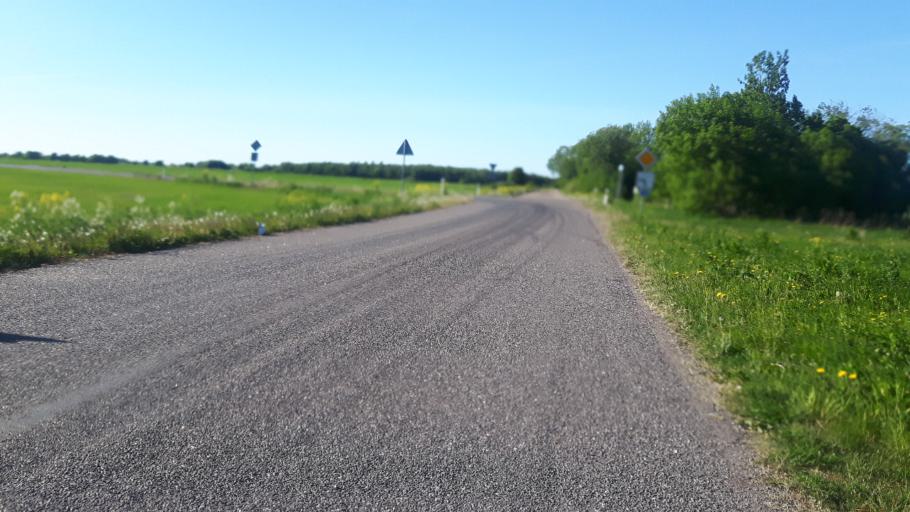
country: EE
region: Ida-Virumaa
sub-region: Kohtla-Jaerve linn
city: Kohtla-Jarve
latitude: 59.4296
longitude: 27.2230
